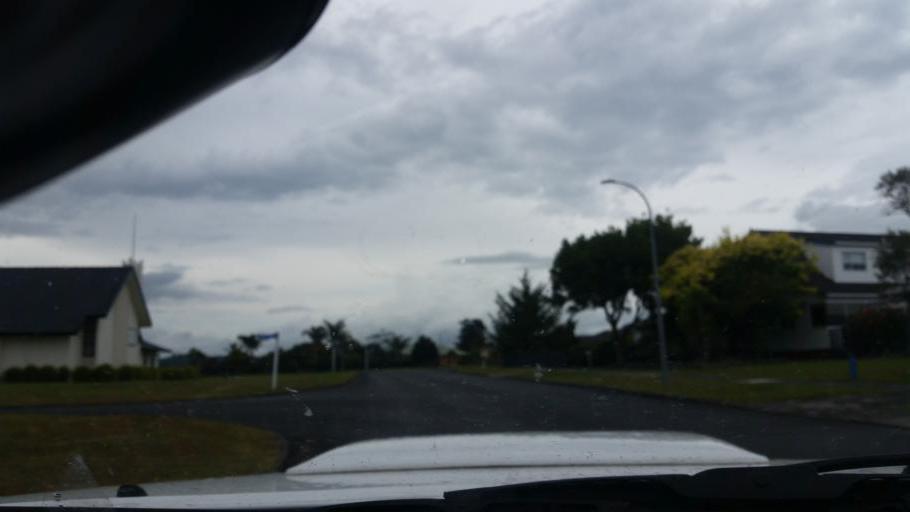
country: NZ
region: Northland
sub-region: Kaipara District
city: Dargaville
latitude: -35.9288
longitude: 173.8642
